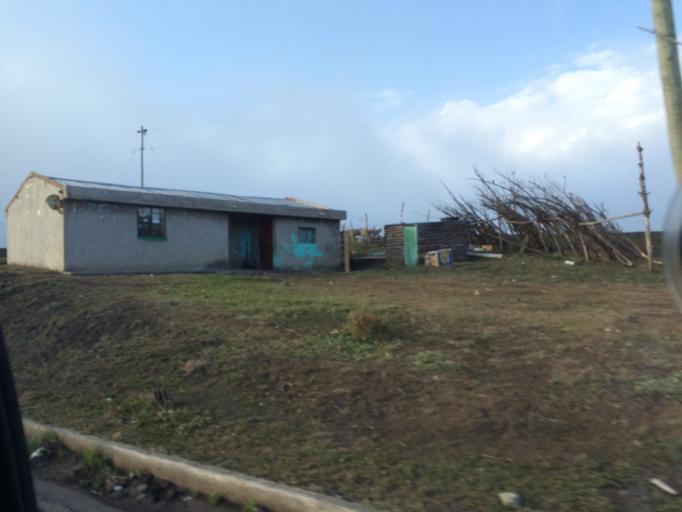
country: EC
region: Chimborazo
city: Alausi
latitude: -2.1301
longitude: -78.7209
